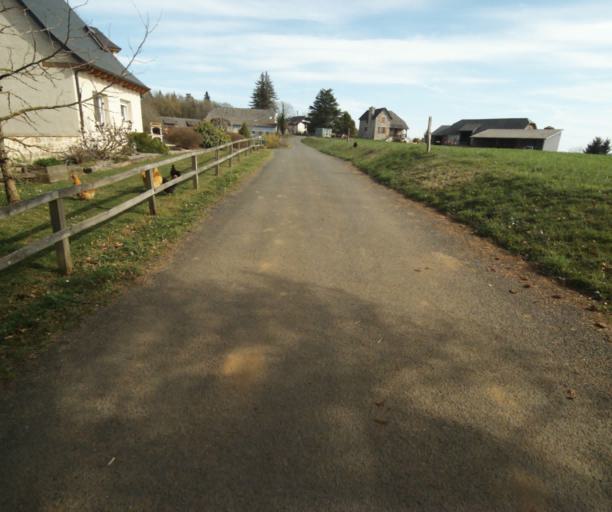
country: FR
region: Limousin
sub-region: Departement de la Correze
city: Naves
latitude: 45.3285
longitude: 1.7459
